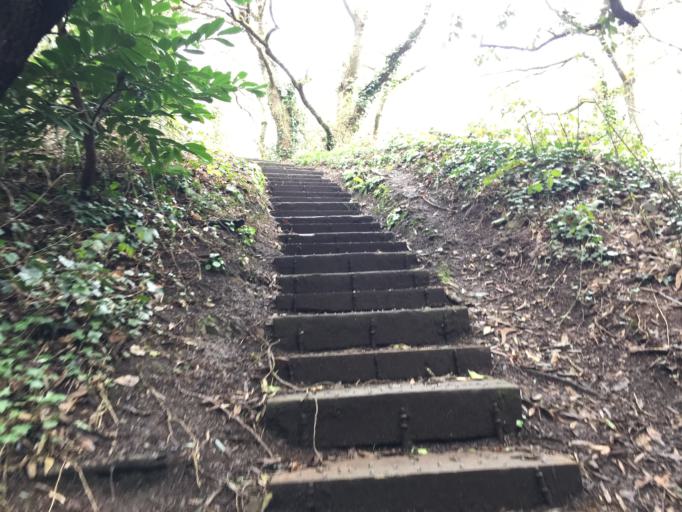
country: JE
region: St Helier
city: Saint Helier
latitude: 49.2157
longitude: -2.1347
